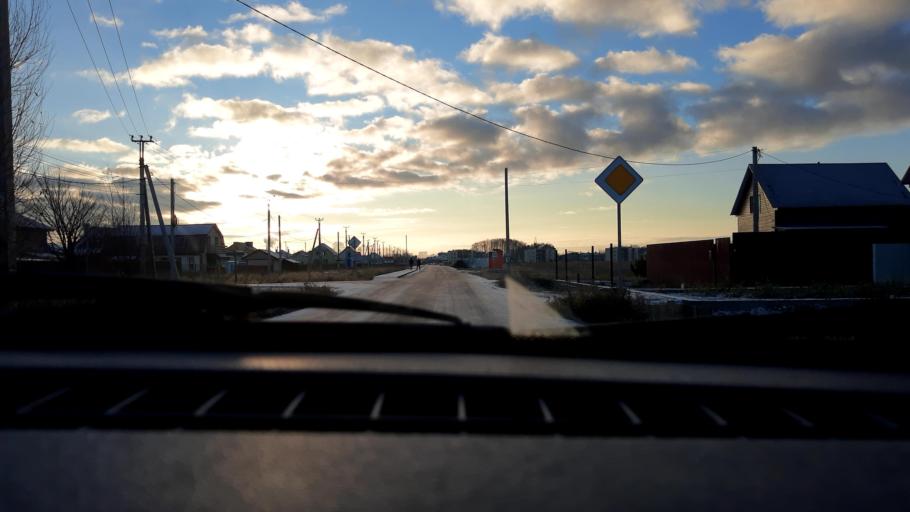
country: RU
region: Bashkortostan
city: Mikhaylovka
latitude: 54.7880
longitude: 55.8276
